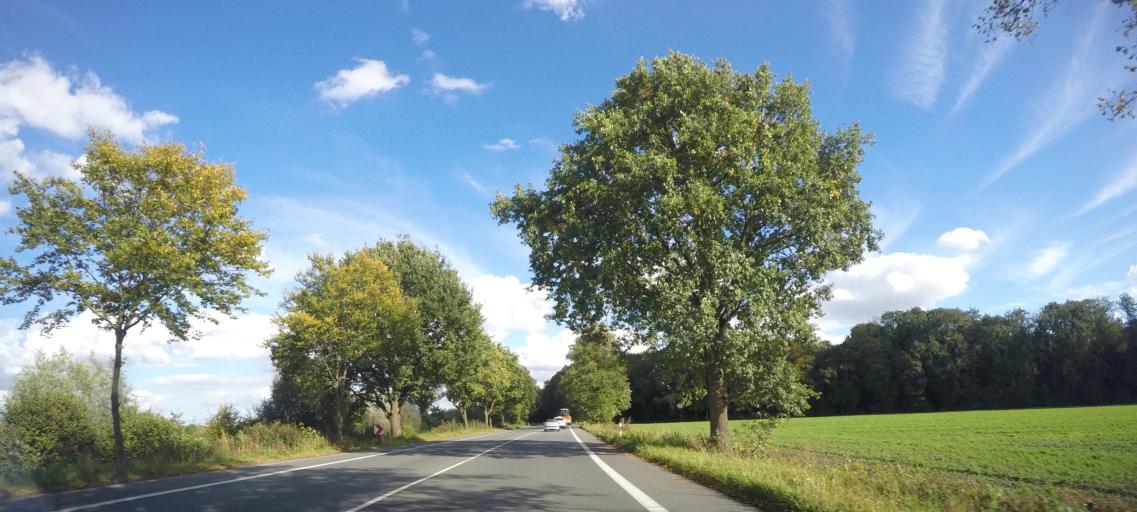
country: DE
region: North Rhine-Westphalia
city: Ahlen
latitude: 51.6999
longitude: 7.9031
